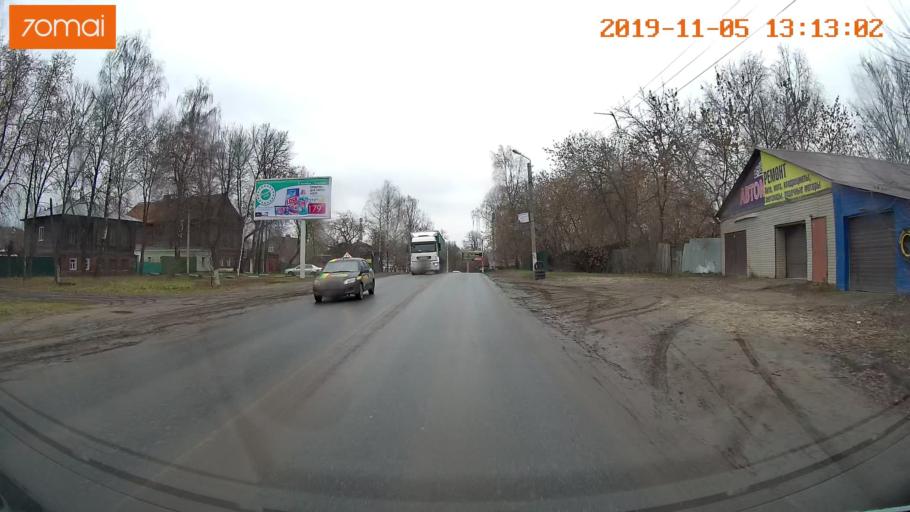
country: RU
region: Ivanovo
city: Shuya
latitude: 56.8537
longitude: 41.3532
